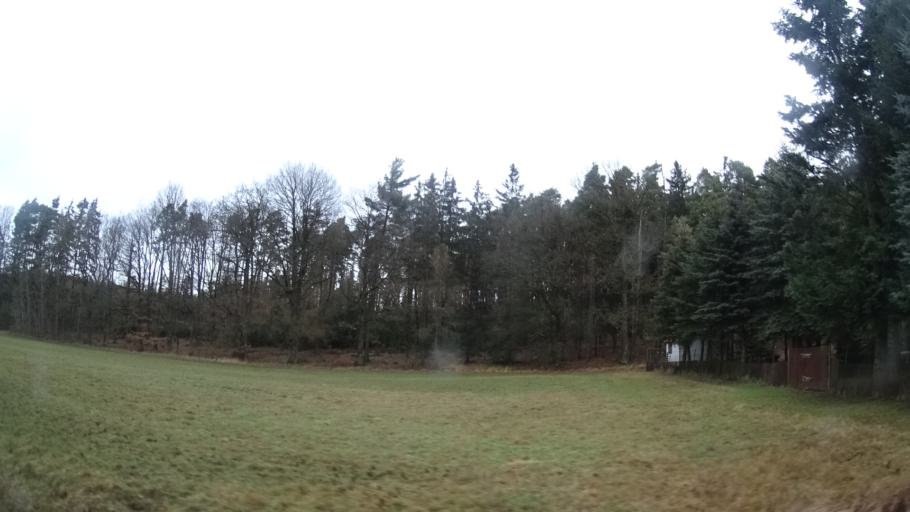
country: DE
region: Thuringia
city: Juchsen
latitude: 50.4599
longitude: 10.4731
